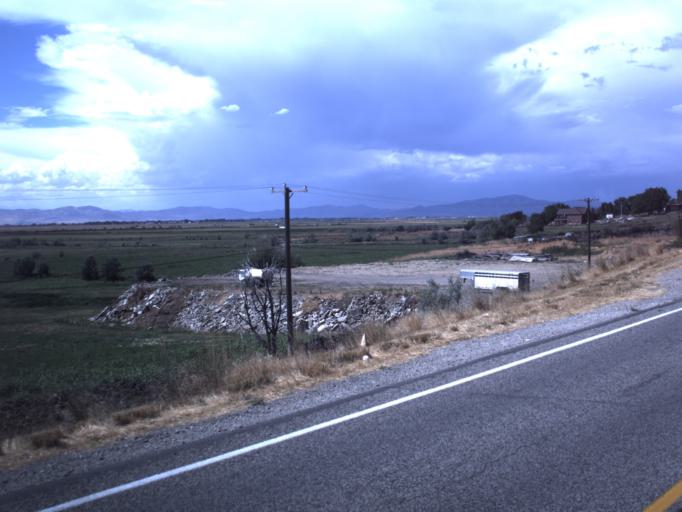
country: US
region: Utah
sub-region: Box Elder County
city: Brigham City
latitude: 41.5539
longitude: -112.0199
